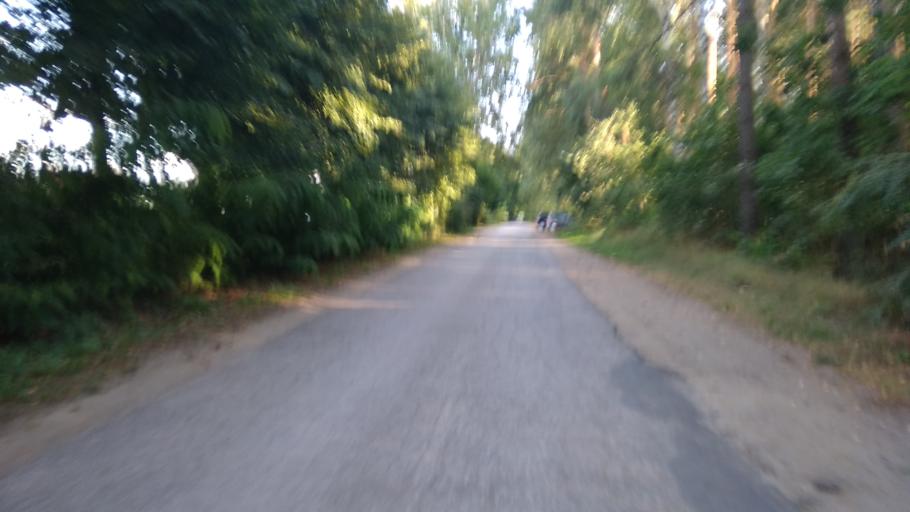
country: PL
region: Kujawsko-Pomorskie
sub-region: Powiat bydgoski
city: Osielsko
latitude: 53.2296
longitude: 18.1190
